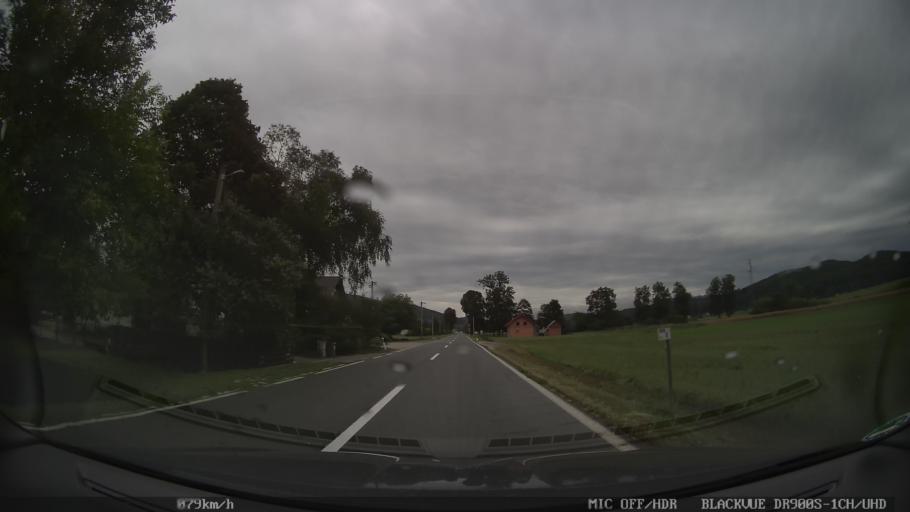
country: HR
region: Licko-Senjska
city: Brinje
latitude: 44.9171
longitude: 15.1544
